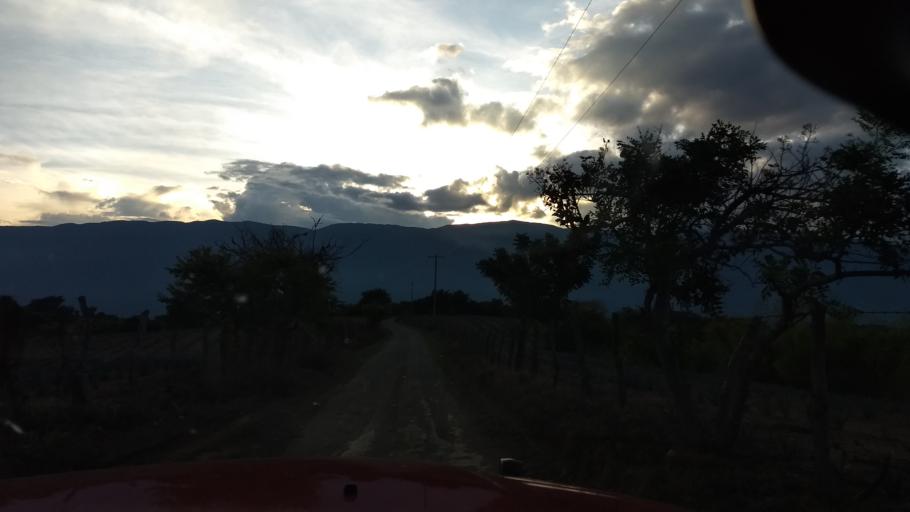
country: MX
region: Colima
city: Suchitlan
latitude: 19.4903
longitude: -103.7885
